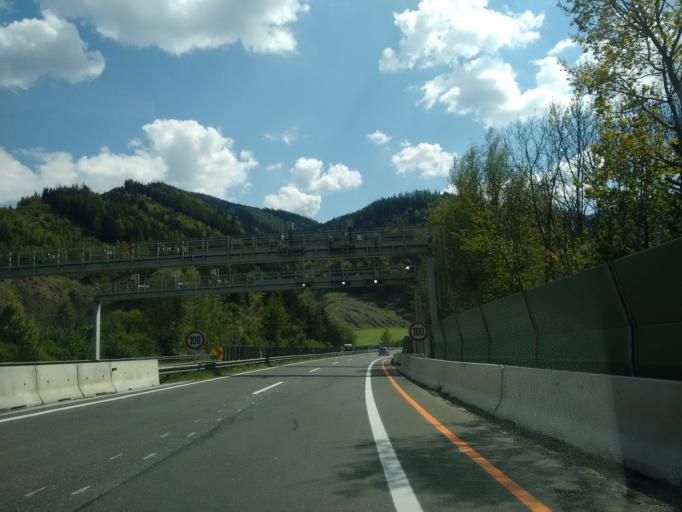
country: AT
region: Styria
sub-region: Politischer Bezirk Leoben
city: Leoben
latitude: 47.3639
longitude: 15.1082
